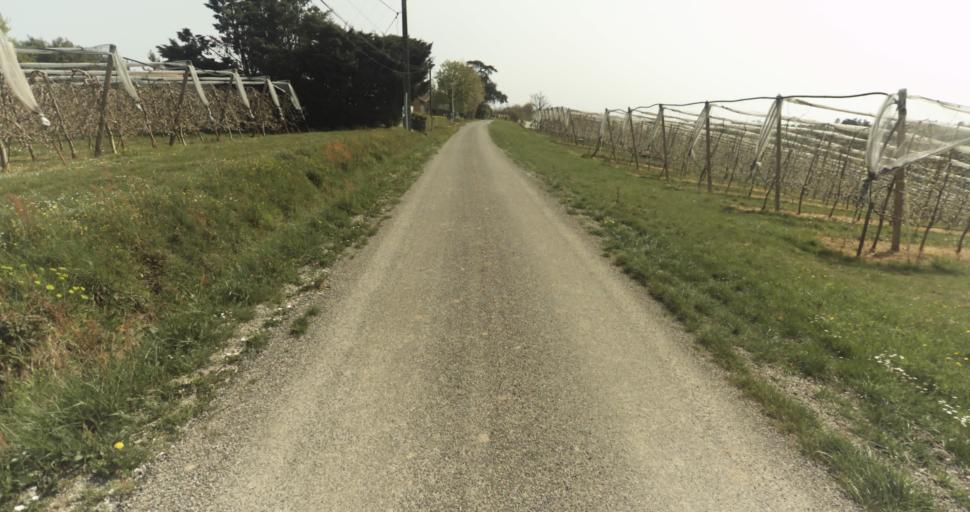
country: FR
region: Midi-Pyrenees
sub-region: Departement du Tarn-et-Garonne
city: Moissac
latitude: 44.1184
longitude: 1.0665
